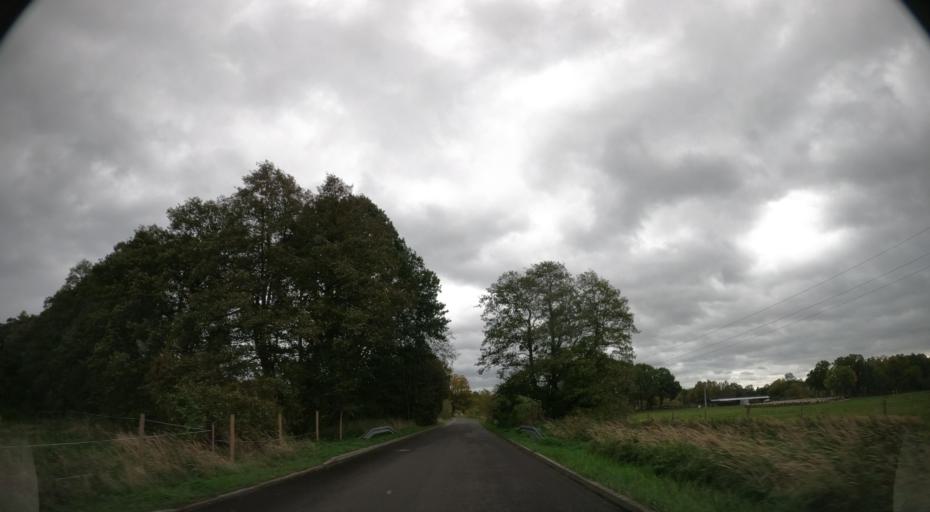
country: PL
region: West Pomeranian Voivodeship
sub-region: Powiat goleniowski
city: Stepnica
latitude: 53.6493
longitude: 14.6451
